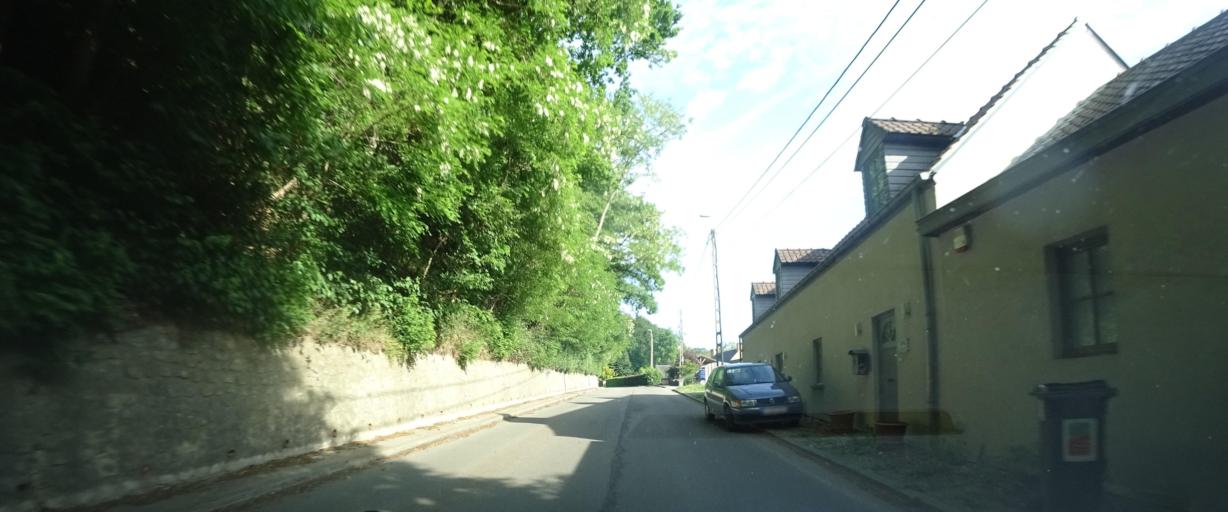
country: BE
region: Wallonia
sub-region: Province du Brabant Wallon
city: Grez-Doiceau
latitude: 50.6993
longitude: 4.6638
